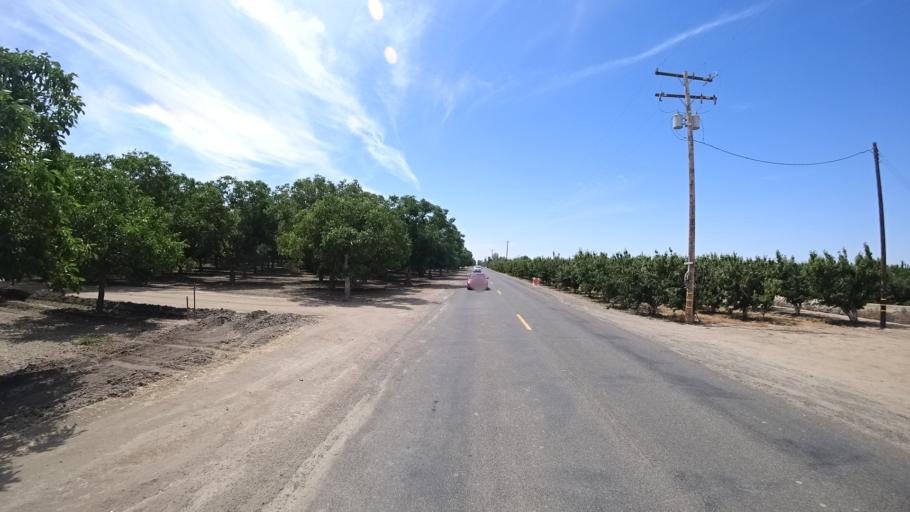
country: US
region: California
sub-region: Kings County
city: Lucerne
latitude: 36.3681
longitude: -119.6910
